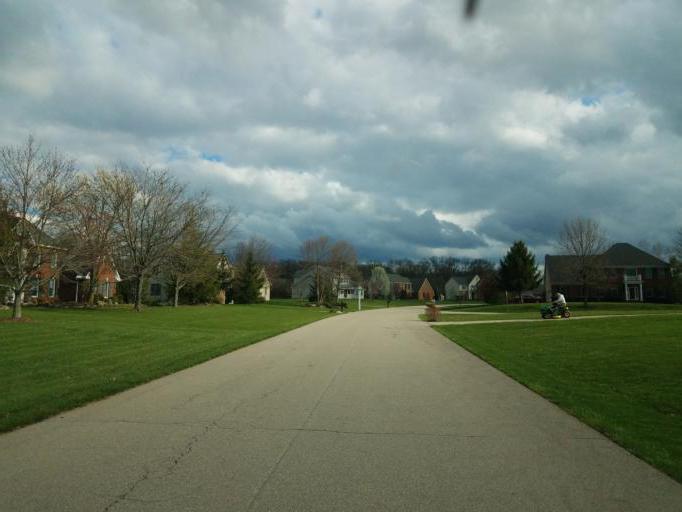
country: US
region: Ohio
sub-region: Delaware County
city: Powell
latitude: 40.1721
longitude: -83.0704
